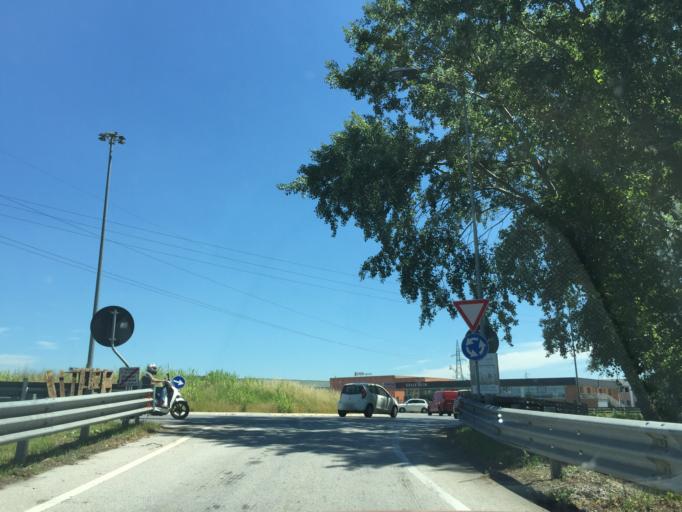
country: IT
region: Tuscany
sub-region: Province of Pisa
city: San Miniato
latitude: 43.6930
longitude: 10.7891
